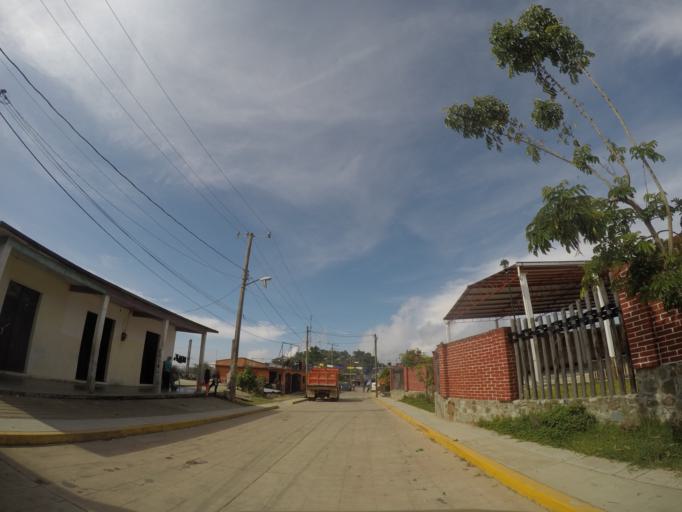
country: MX
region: Oaxaca
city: Pluma Hidalgo
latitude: 15.9288
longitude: -96.4173
